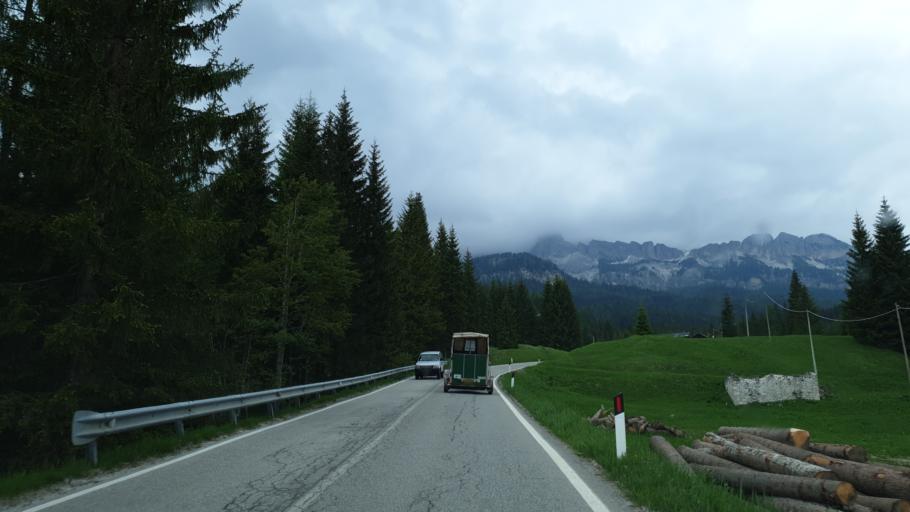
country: IT
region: Veneto
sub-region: Provincia di Belluno
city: San Vito
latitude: 46.5442
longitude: 12.2510
